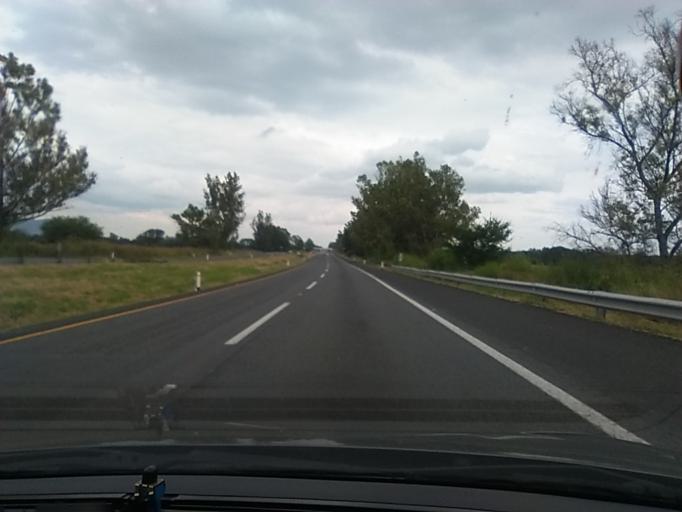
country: MX
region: Jalisco
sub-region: Ocotlan
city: Joconoxtle (La Tuna)
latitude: 20.3815
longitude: -102.7004
